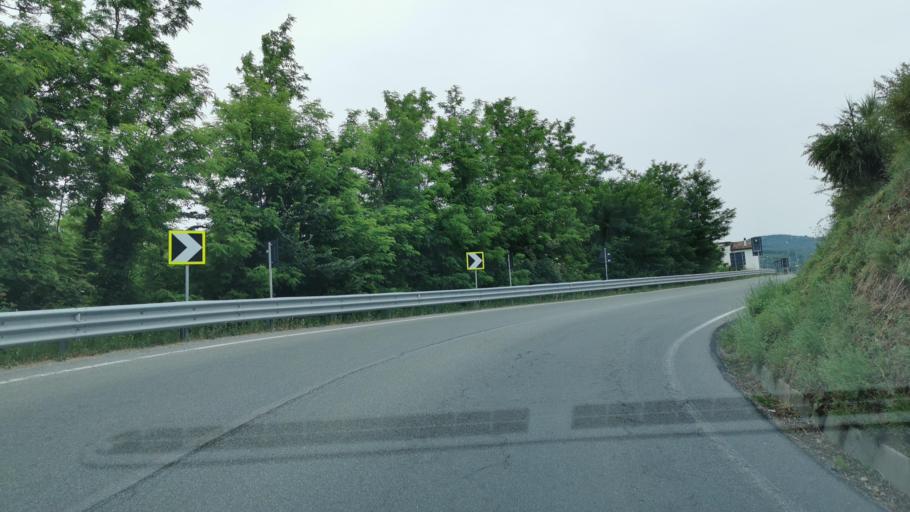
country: IT
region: Piedmont
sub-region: Provincia di Cuneo
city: Ceva
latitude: 44.3796
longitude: 8.0418
